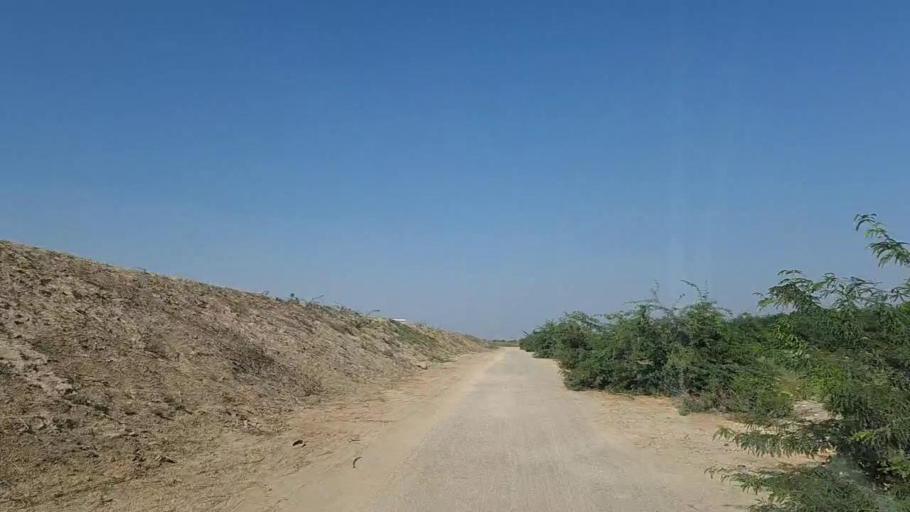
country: PK
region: Sindh
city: Chuhar Jamali
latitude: 24.5699
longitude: 68.0300
